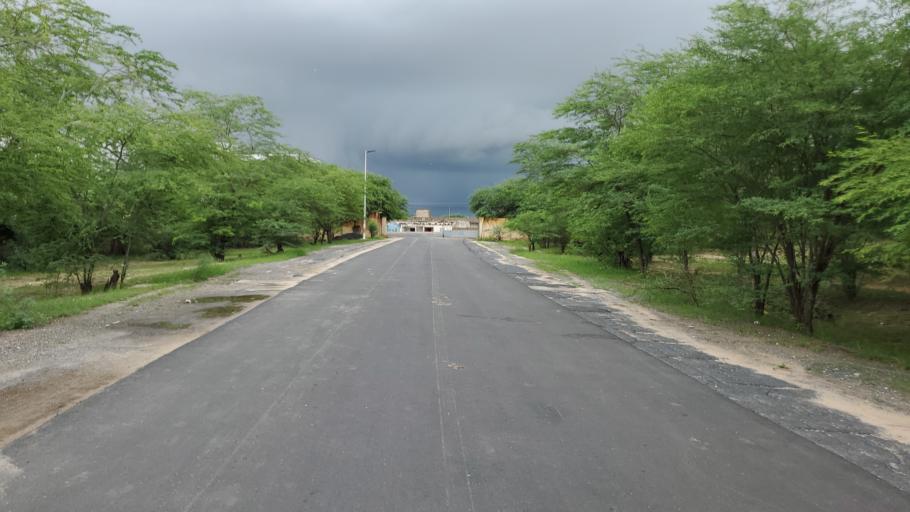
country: SN
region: Saint-Louis
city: Saint-Louis
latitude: 16.0618
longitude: -16.4188
